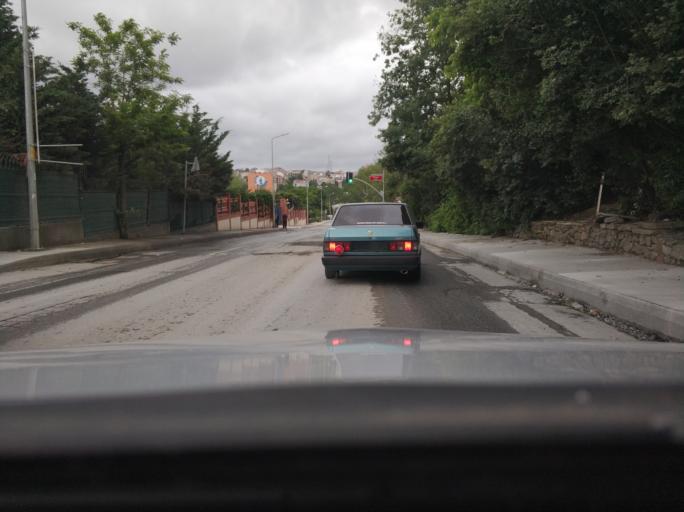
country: TR
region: Istanbul
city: Kemerburgaz
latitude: 41.1610
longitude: 28.9014
